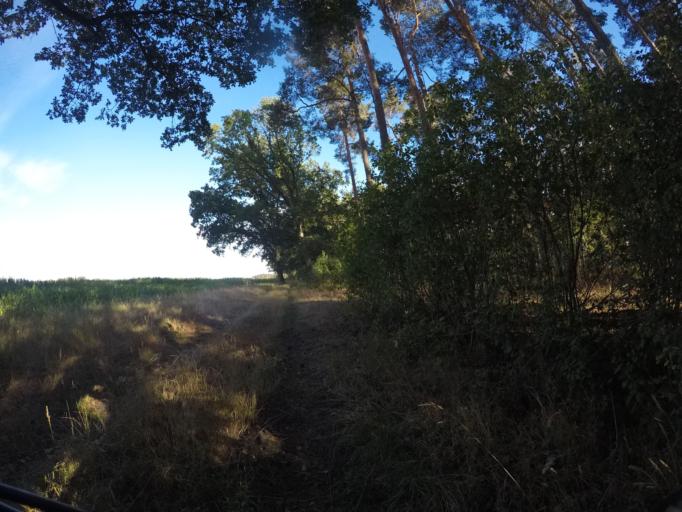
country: DE
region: Lower Saxony
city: Hitzacker
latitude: 53.2265
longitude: 11.0500
